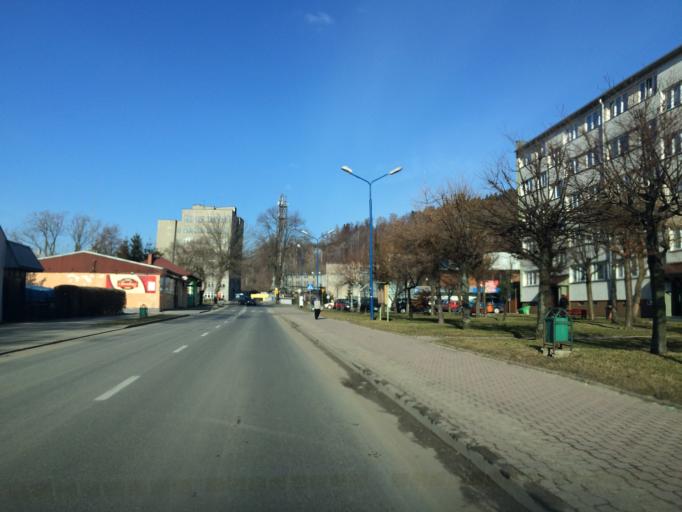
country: PL
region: Lower Silesian Voivodeship
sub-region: Powiat klodzki
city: Stronie Slaskie
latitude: 50.2980
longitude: 16.8751
